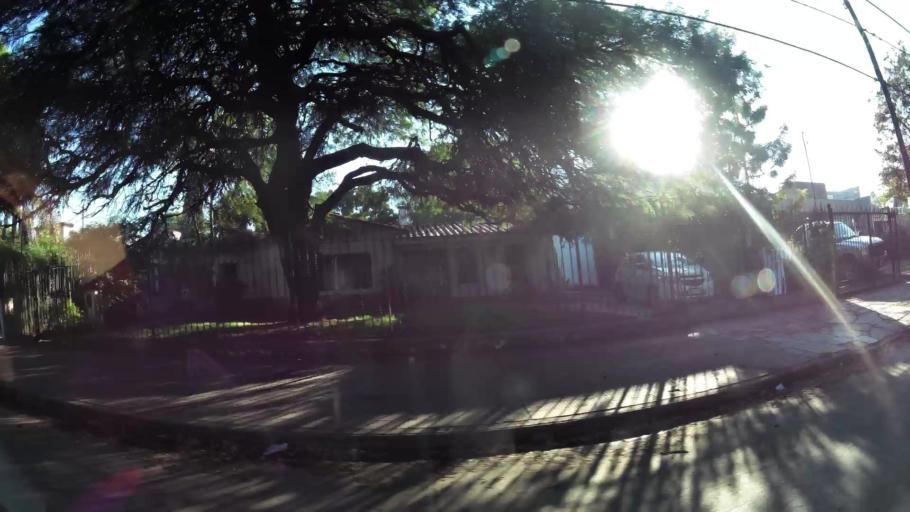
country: AR
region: Cordoba
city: Villa Allende
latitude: -31.3520
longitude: -64.2468
